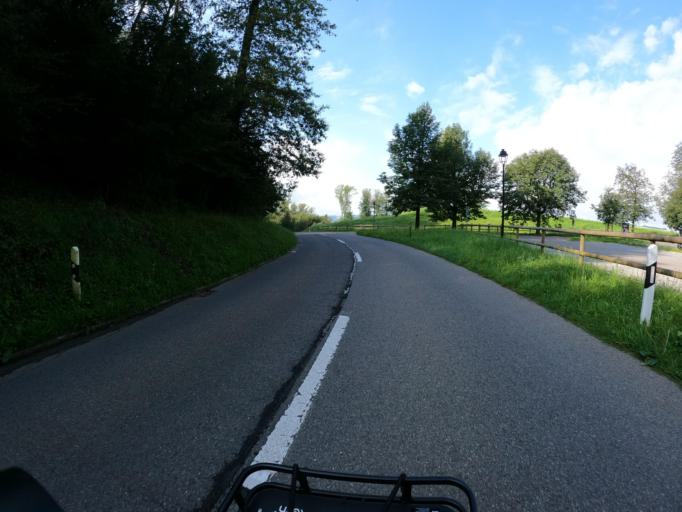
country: CH
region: Lucerne
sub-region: Hochdorf District
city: Hitzkirch
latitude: 47.2158
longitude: 8.2762
